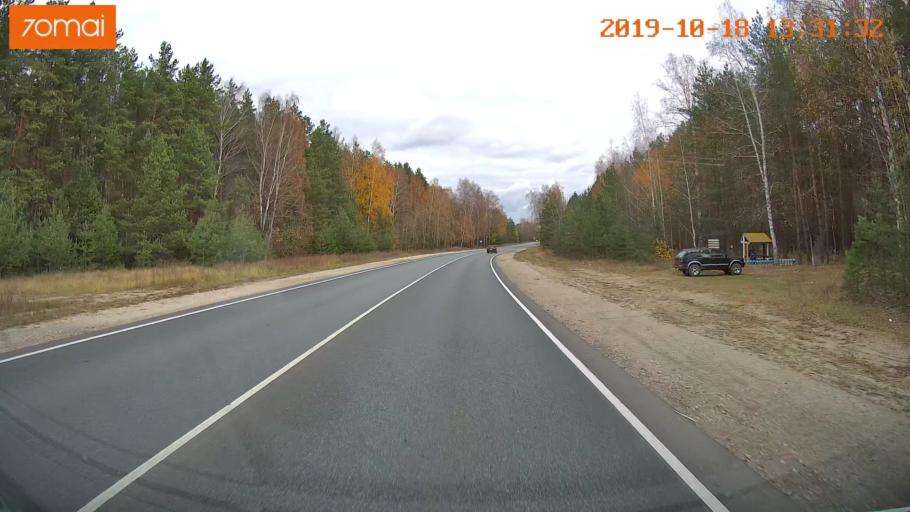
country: RU
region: Rjazan
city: Solotcha
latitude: 54.8233
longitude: 39.9018
